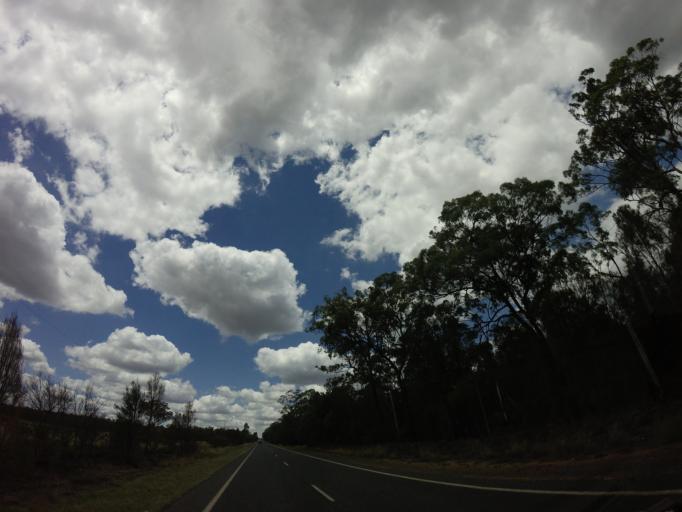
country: AU
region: Queensland
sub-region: Goondiwindi
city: Goondiwindi
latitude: -28.0043
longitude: 150.9308
